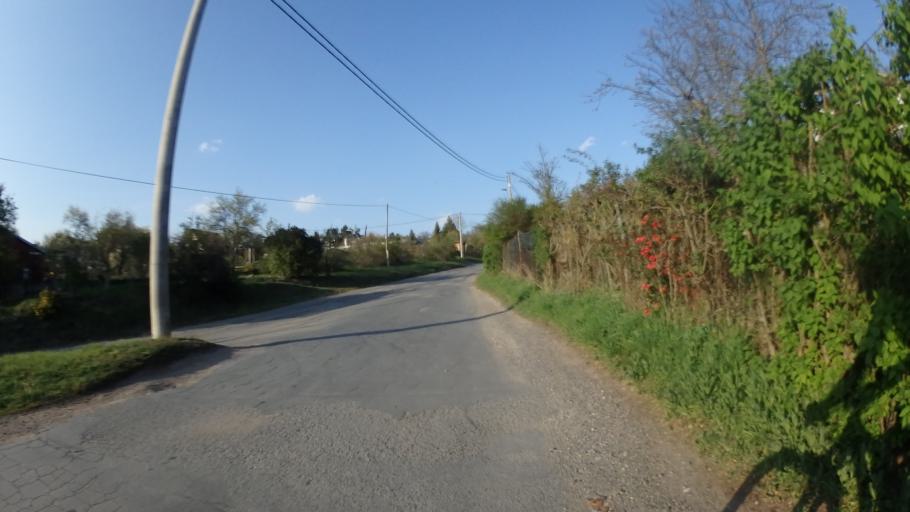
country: CZ
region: South Moravian
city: Moravany
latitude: 49.1780
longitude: 16.5791
